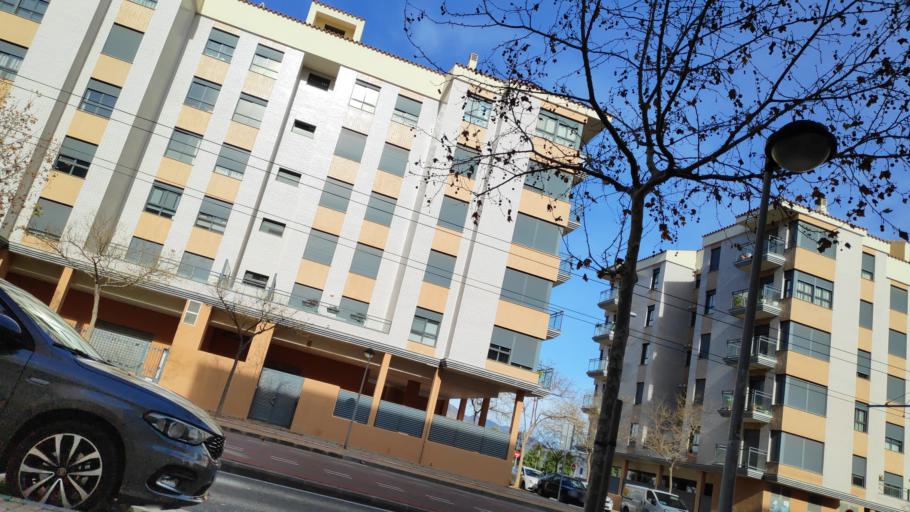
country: ES
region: Valencia
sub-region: Provincia de Castello
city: Castello de la Plana
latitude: 39.9916
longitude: -0.0587
